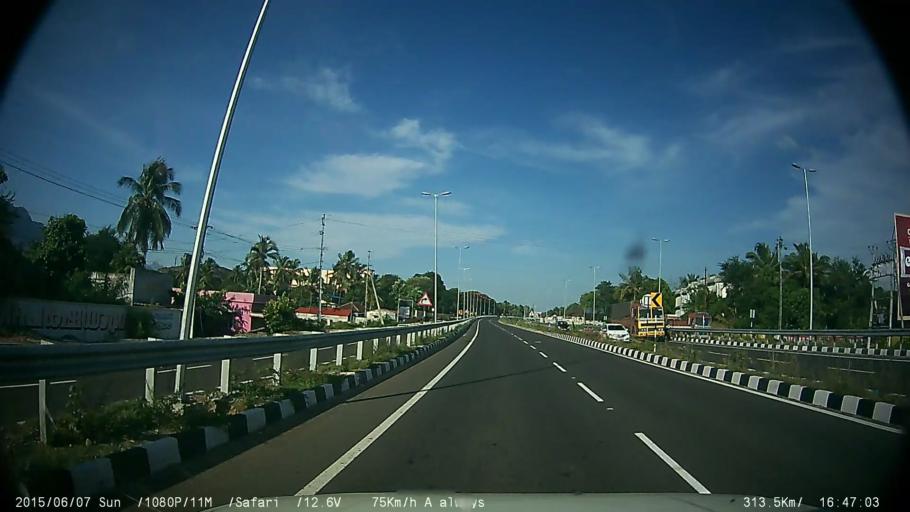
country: IN
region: Kerala
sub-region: Palakkad district
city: Chittur
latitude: 10.7971
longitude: 76.7651
